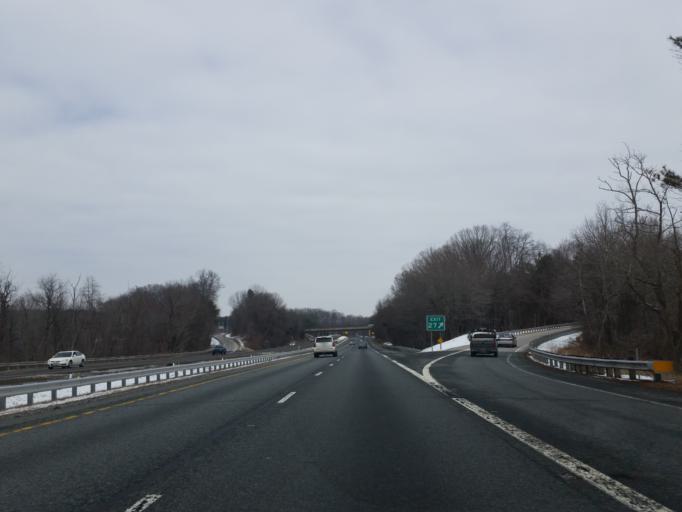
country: US
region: Maryland
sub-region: Baltimore County
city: Hunt Valley
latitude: 39.5872
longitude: -76.6756
